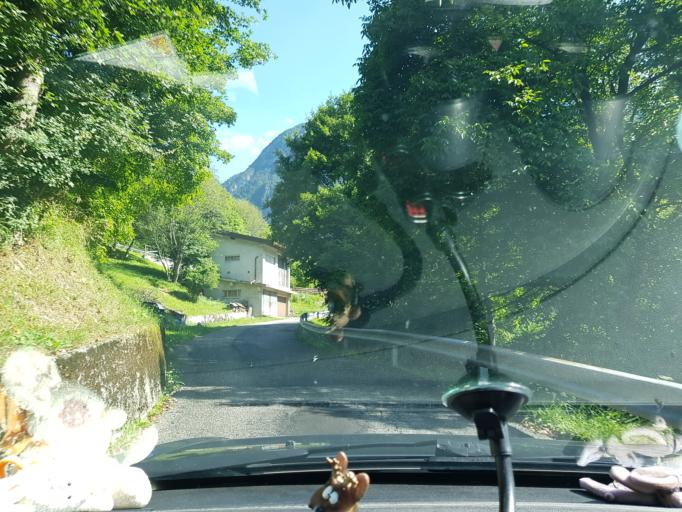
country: IT
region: Friuli Venezia Giulia
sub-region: Provincia di Udine
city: Dogna
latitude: 46.4467
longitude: 13.3124
